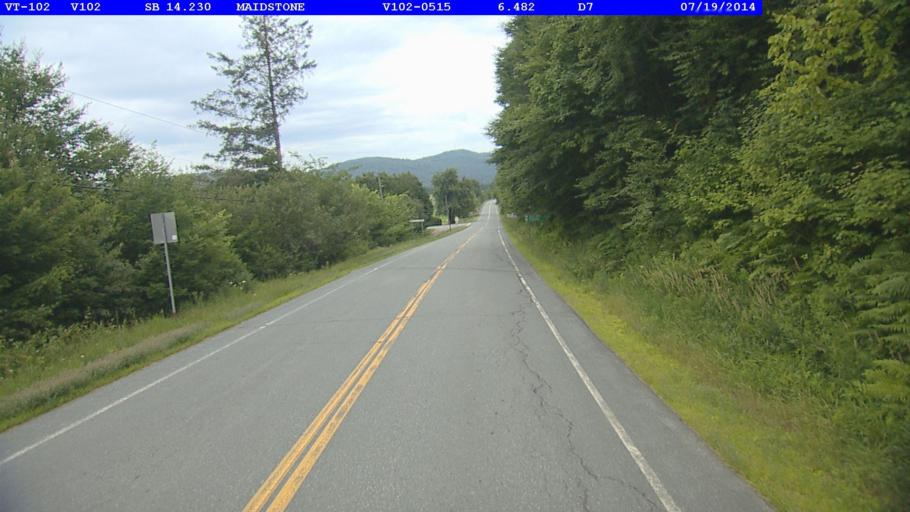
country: US
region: New Hampshire
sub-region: Coos County
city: Stratford
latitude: 44.6491
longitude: -71.5754
